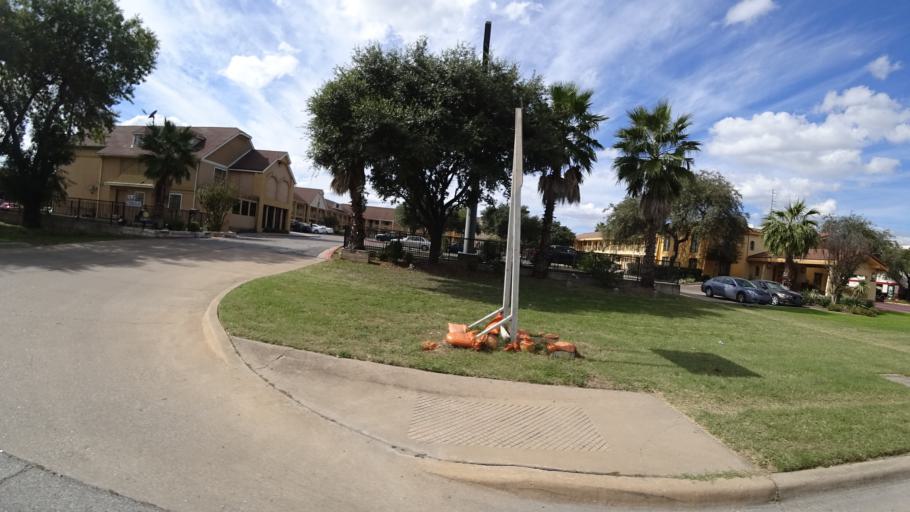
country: US
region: Texas
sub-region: Travis County
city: Austin
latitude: 30.2144
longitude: -97.7534
